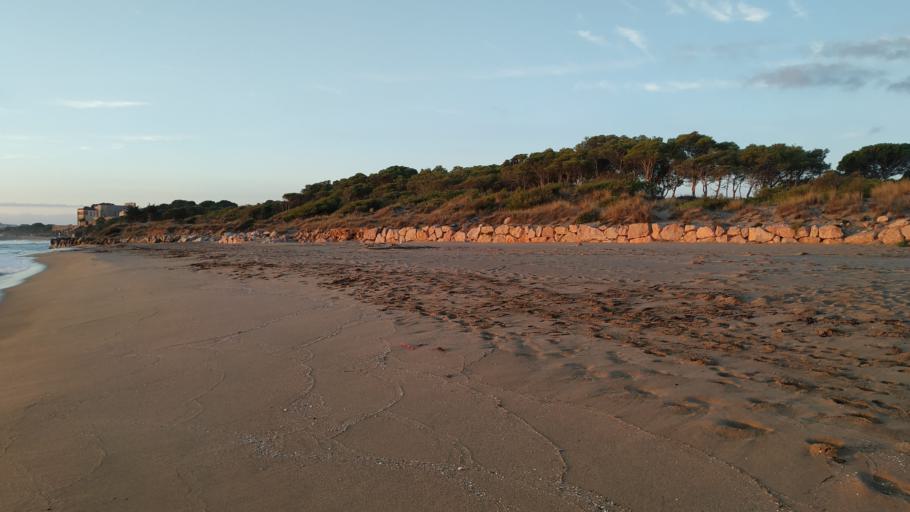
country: ES
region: Catalonia
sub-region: Provincia de Girona
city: l'Escala
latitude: 42.1454
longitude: 3.1166
